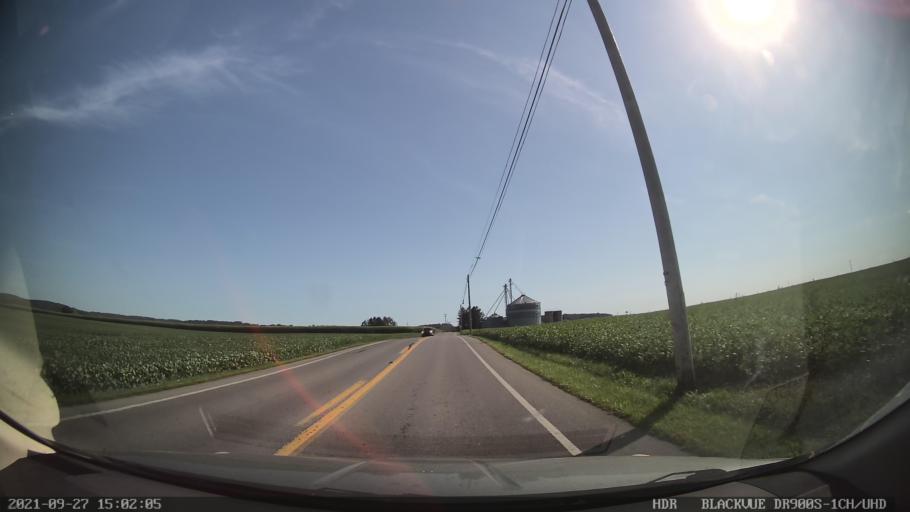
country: US
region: Pennsylvania
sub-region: Berks County
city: Kutztown
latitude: 40.4870
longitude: -75.7595
